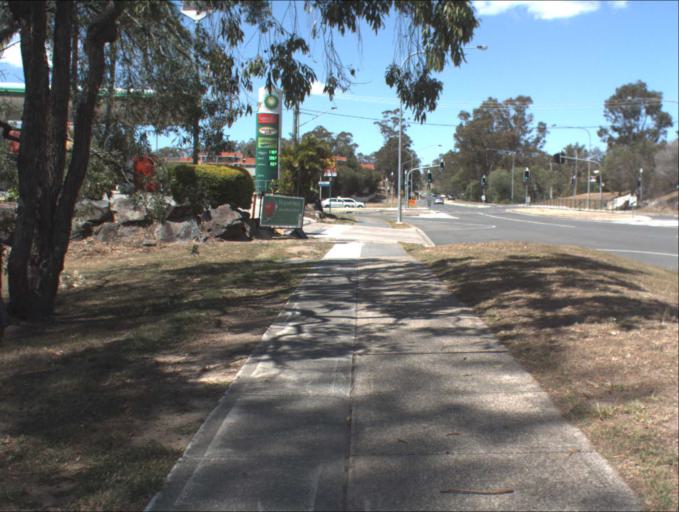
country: AU
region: Queensland
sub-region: Logan
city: Windaroo
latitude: -27.7223
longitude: 153.1949
